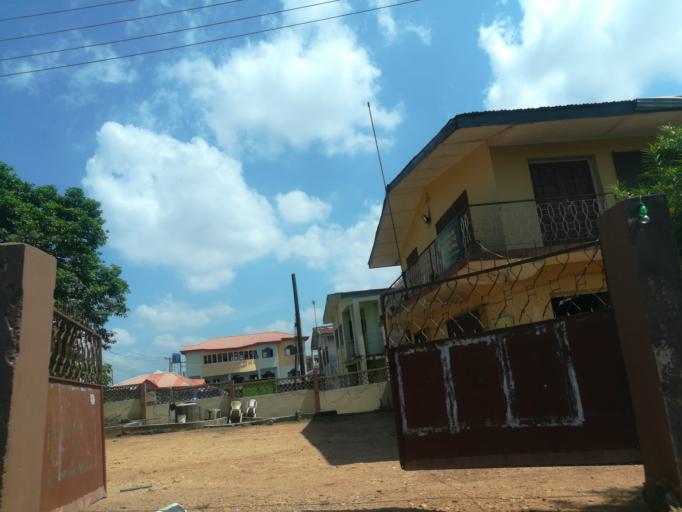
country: NG
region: Oyo
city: Ibadan
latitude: 7.3541
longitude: 3.8648
